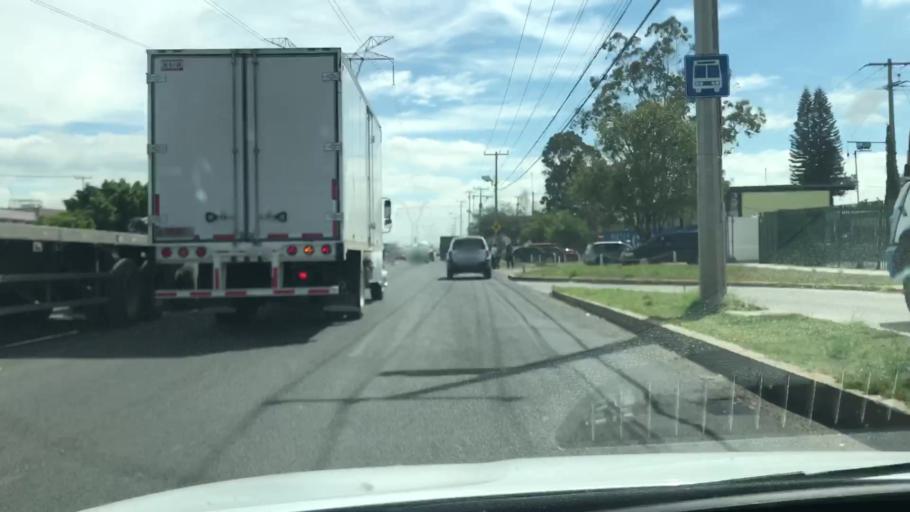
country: MX
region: Guanajuato
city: Celaya
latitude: 20.5514
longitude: -100.8123
